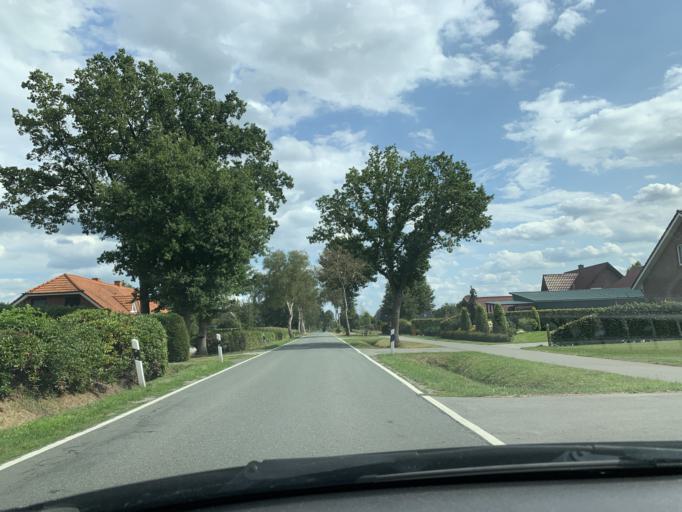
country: DE
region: Lower Saxony
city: Apen
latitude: 53.2685
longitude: 7.8322
